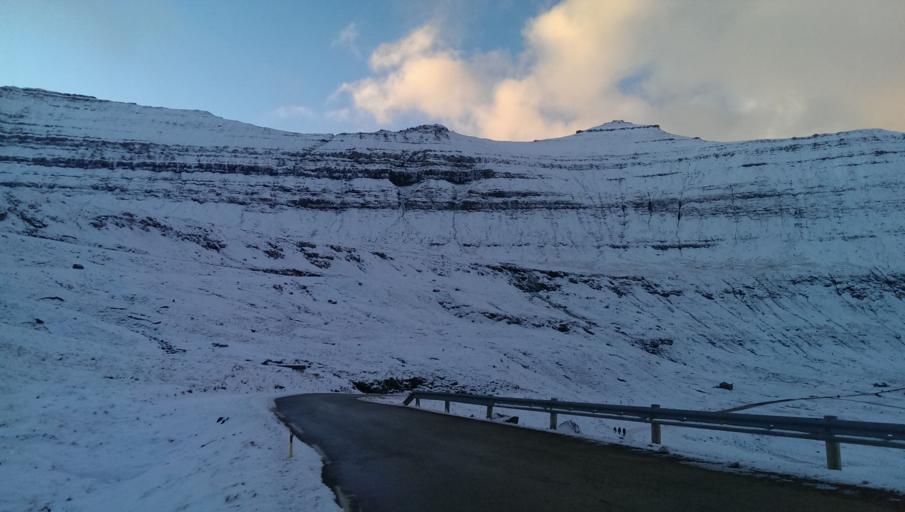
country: FO
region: Eysturoy
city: Fuglafjordur
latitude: 62.2549
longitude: -6.8582
